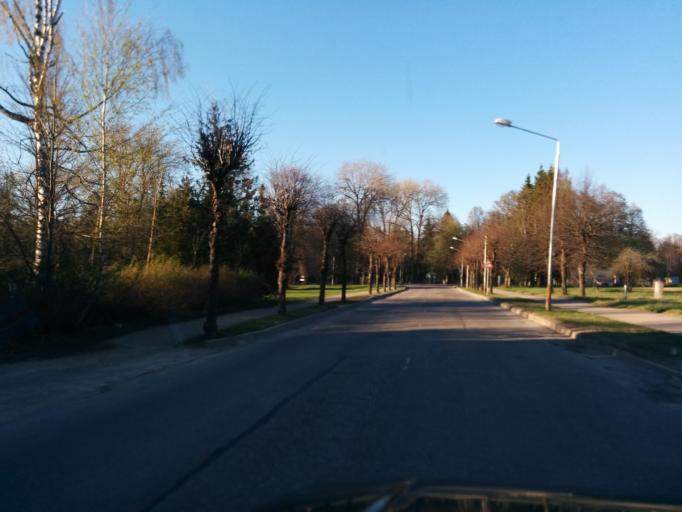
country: LV
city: Tireli
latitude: 56.9464
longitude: 23.5006
